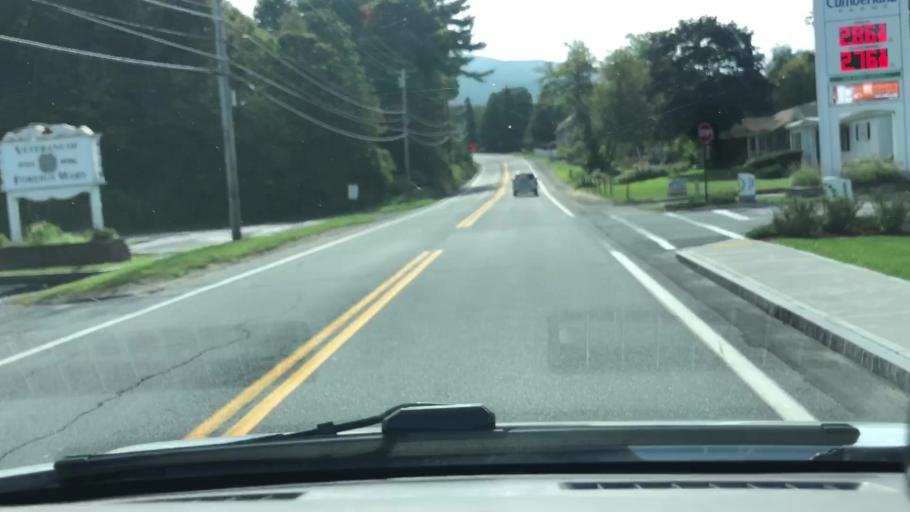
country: US
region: Massachusetts
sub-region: Berkshire County
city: North Adams
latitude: 42.6973
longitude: -73.0909
